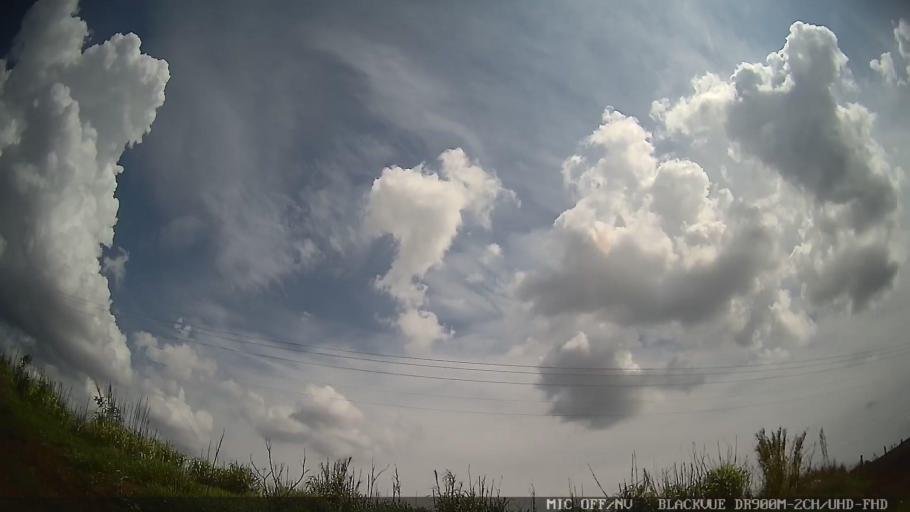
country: BR
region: Sao Paulo
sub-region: Braganca Paulista
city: Braganca Paulista
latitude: -22.9445
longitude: -46.6742
